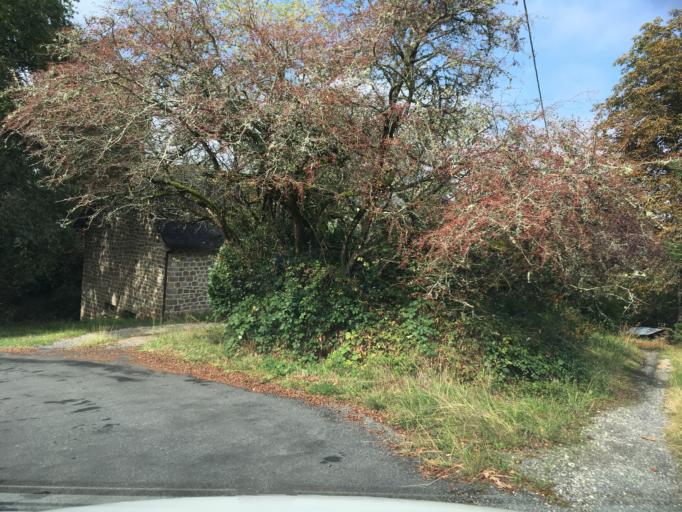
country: FR
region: Limousin
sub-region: Departement de la Correze
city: Brive-la-Gaillarde
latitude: 45.1434
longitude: 1.5140
